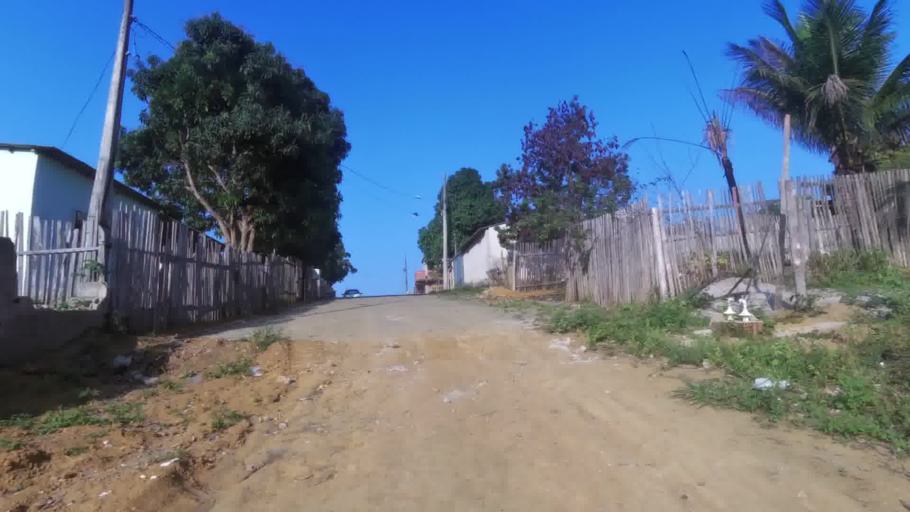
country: BR
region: Espirito Santo
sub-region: Piuma
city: Piuma
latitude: -20.8244
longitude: -40.7220
